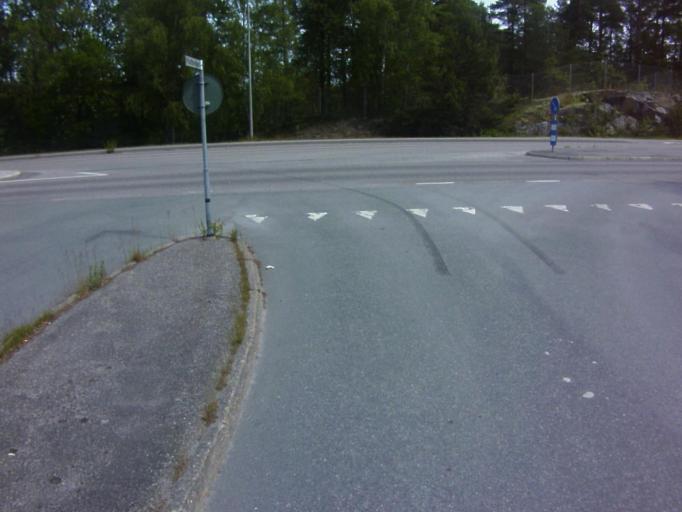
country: SE
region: Soedermanland
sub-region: Eskilstuna Kommun
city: Eskilstuna
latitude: 59.3560
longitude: 16.5286
